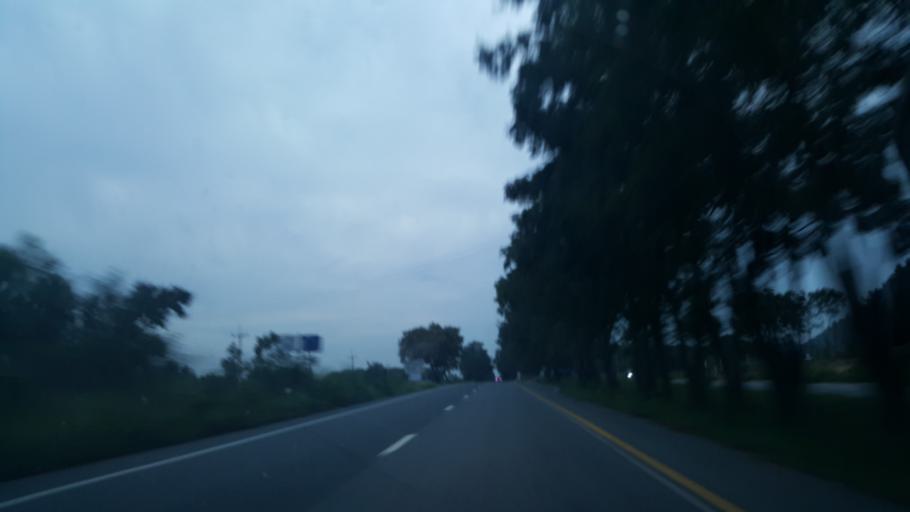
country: TH
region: Rayong
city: Ban Chang
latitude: 12.7782
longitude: 100.9919
